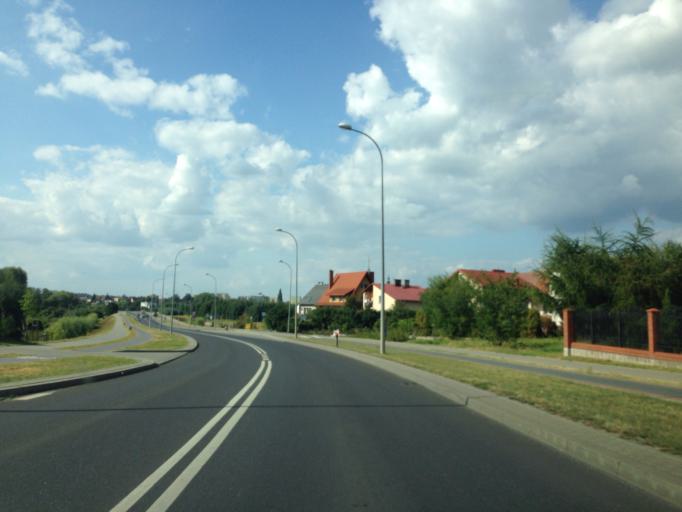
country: PL
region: Warmian-Masurian Voivodeship
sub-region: Powiat ilawski
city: Ilawa
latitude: 53.5972
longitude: 19.5769
